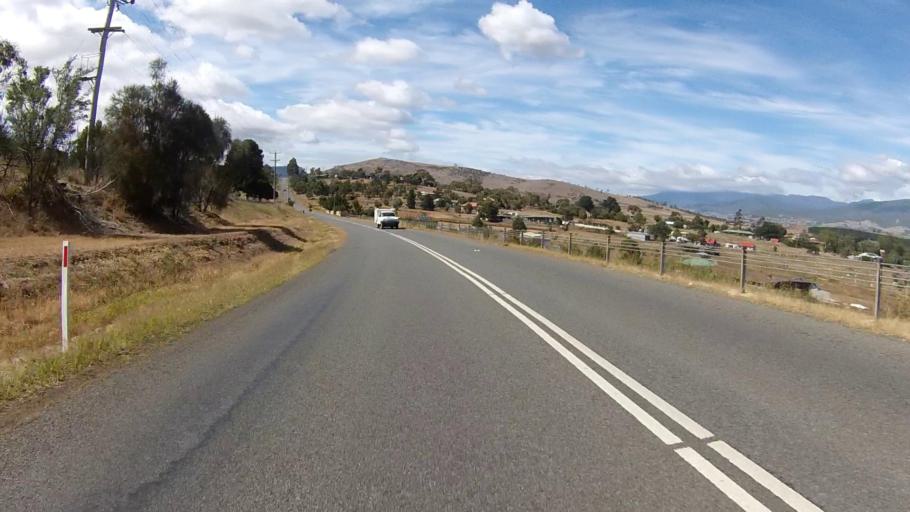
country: AU
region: Tasmania
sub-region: Brighton
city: Bridgewater
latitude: -42.7095
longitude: 147.2692
